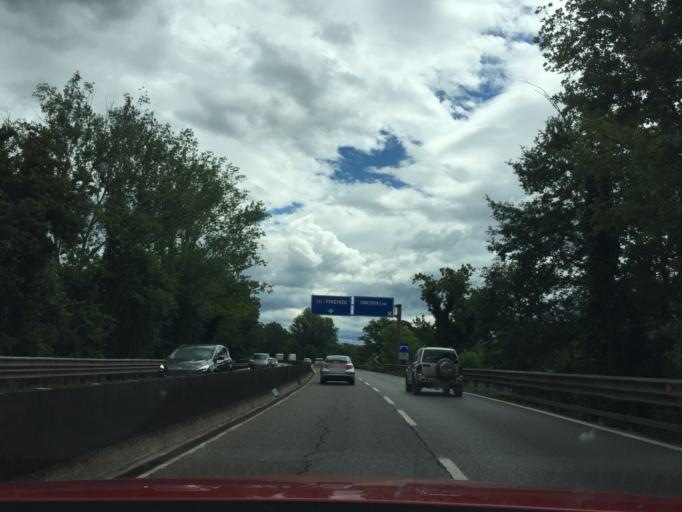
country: IT
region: Tuscany
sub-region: Province of Florence
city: Ginestra Fiorentina
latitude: 43.7114
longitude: 11.0516
